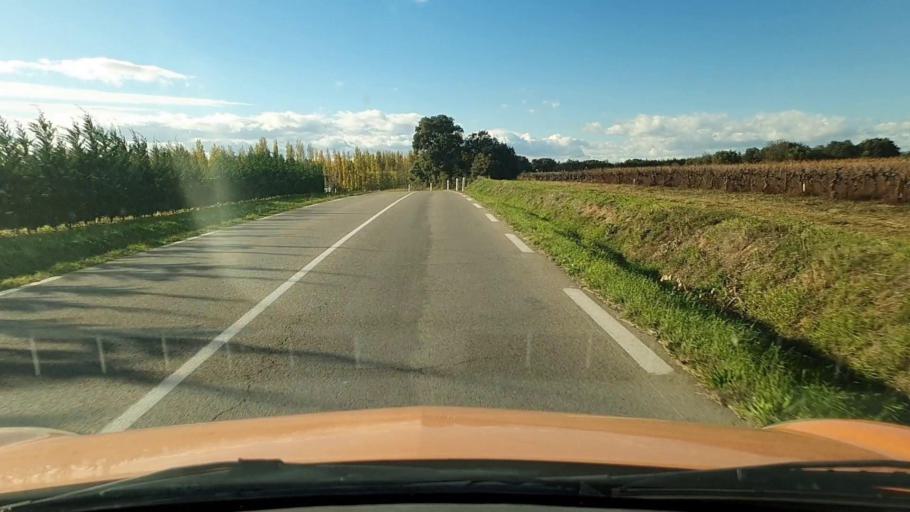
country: FR
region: Languedoc-Roussillon
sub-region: Departement du Gard
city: Vauvert
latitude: 43.6553
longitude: 4.2910
